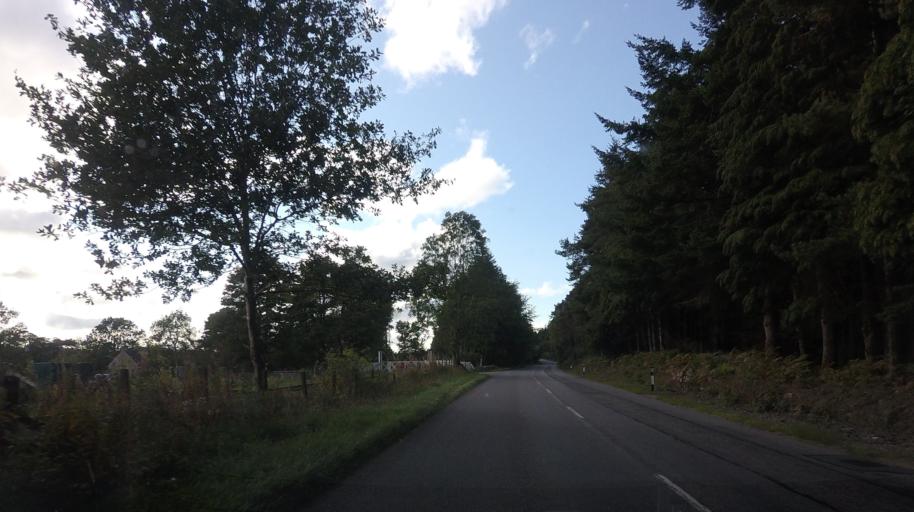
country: GB
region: Scotland
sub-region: Aberdeenshire
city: Banchory
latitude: 57.0574
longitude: -2.4506
